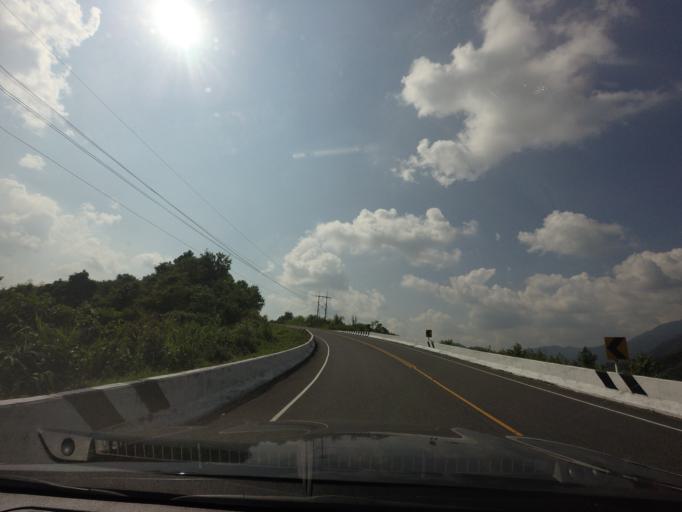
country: TH
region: Nan
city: Santi Suk
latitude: 18.9739
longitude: 101.0346
